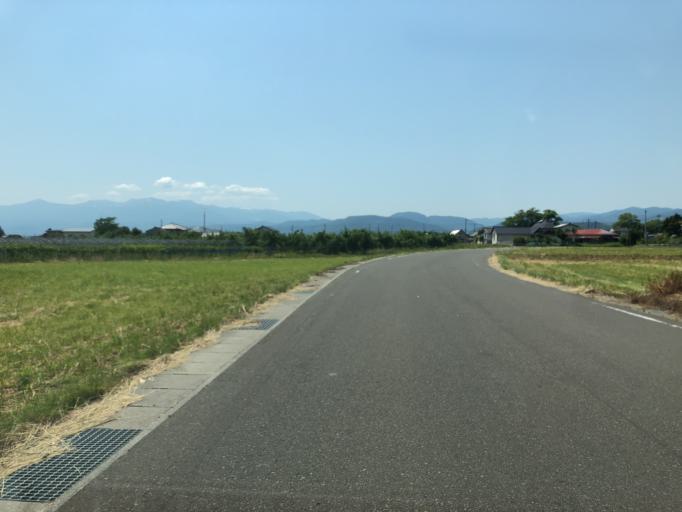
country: JP
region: Fukushima
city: Hobaramachi
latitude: 37.8194
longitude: 140.4827
